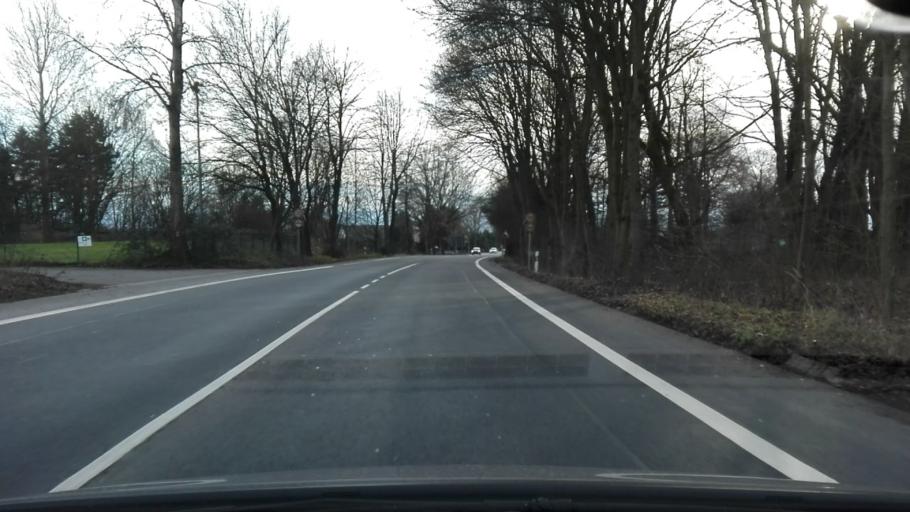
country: DE
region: North Rhine-Westphalia
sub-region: Regierungsbezirk Arnsberg
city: Unna
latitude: 51.4991
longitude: 7.7039
